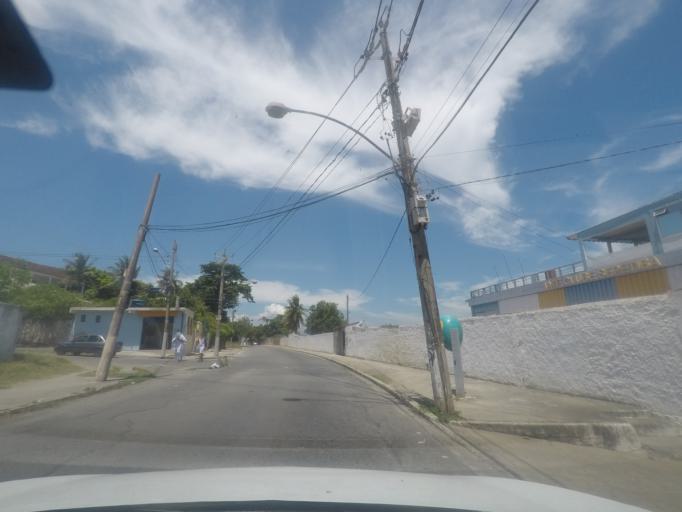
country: BR
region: Rio de Janeiro
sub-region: Itaguai
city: Itaguai
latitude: -22.9855
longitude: -43.6985
